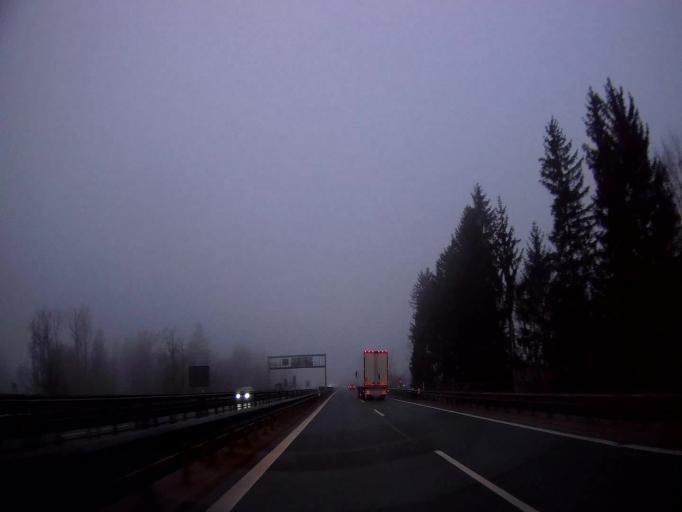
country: DE
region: Bavaria
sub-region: Upper Bavaria
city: Piding
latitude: 47.7679
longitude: 12.9253
